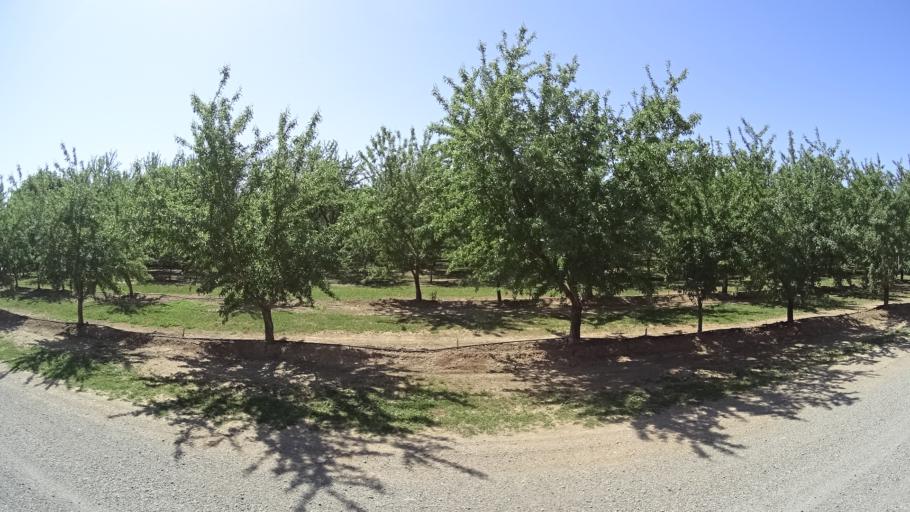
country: US
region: California
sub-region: Glenn County
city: Orland
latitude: 39.7654
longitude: -122.1821
